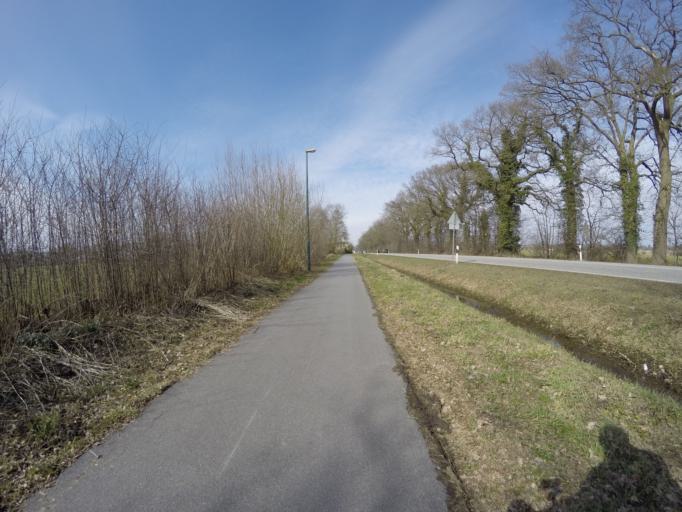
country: DE
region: Schleswig-Holstein
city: Bilsen
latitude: 53.7618
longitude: 9.8794
